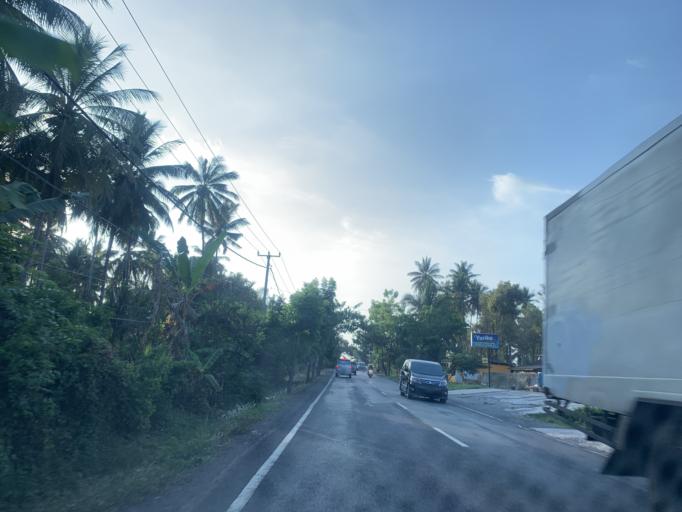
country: ID
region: Bali
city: Banjar Delodrurung
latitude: -8.4920
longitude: 114.9573
